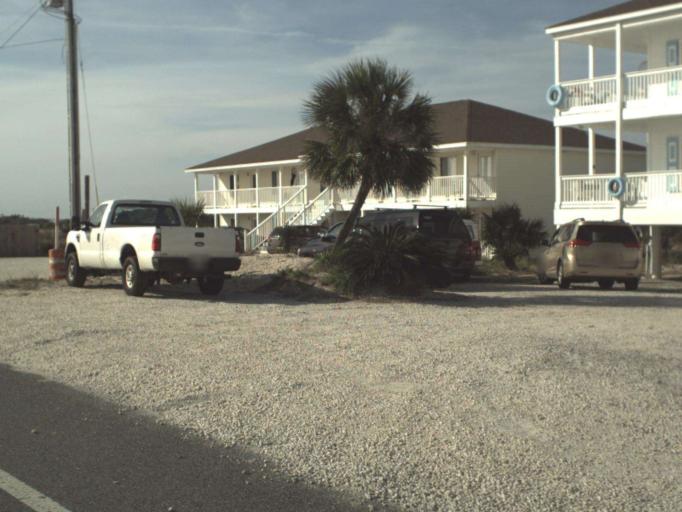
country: US
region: Alabama
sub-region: Baldwin County
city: Orange Beach
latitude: 30.2949
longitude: -87.4459
